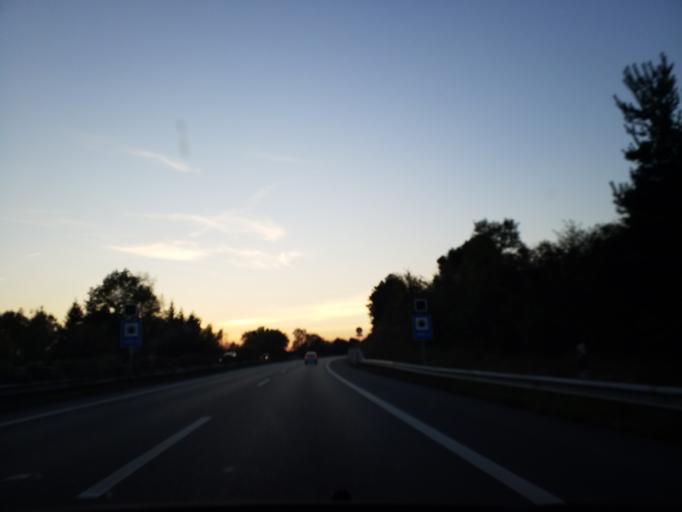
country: CH
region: Vaud
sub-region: Lavaux-Oron District
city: Chexbres
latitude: 46.4823
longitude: 6.7853
